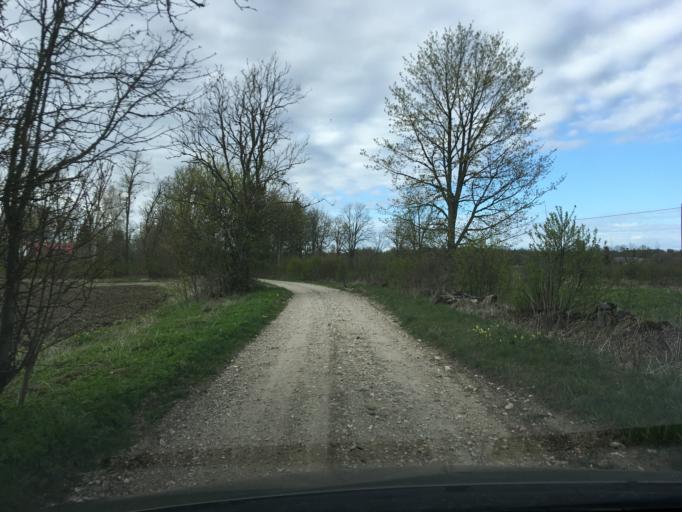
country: EE
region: Laeaene
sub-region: Lihula vald
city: Lihula
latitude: 58.5752
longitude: 23.7236
